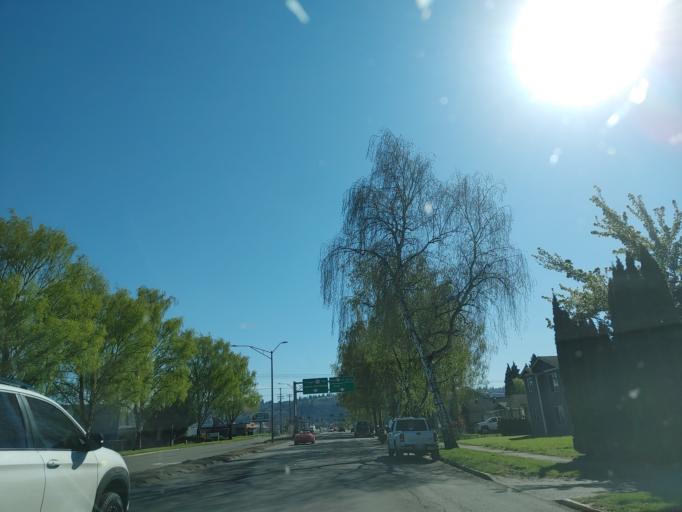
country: US
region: Washington
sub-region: Cowlitz County
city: Longview
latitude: 46.1189
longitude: -122.9485
